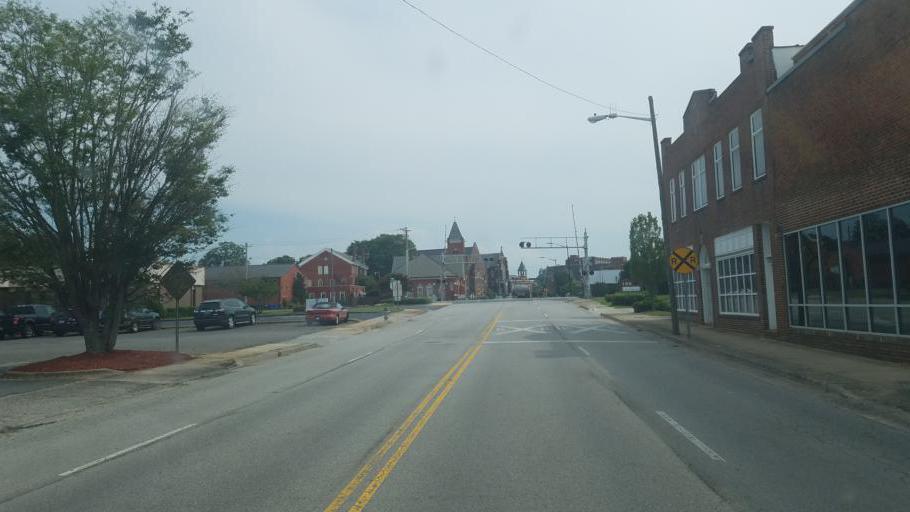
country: US
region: South Carolina
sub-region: York County
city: Rock Hill
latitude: 34.9282
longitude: -81.0238
